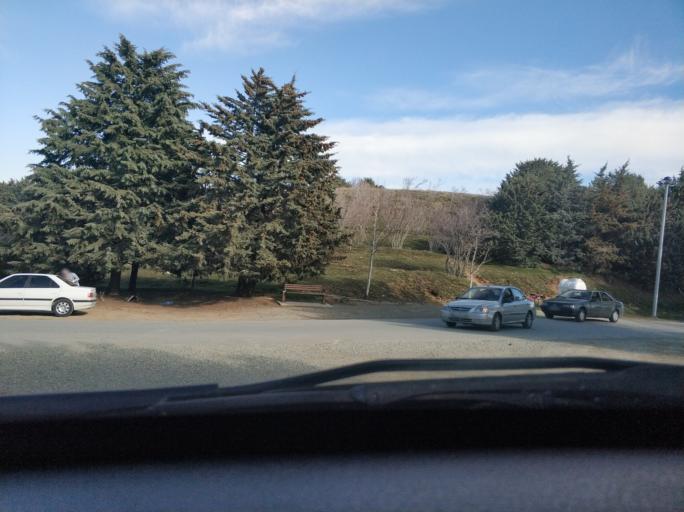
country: IR
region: Tehran
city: Tajrish
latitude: 35.8020
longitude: 51.5672
